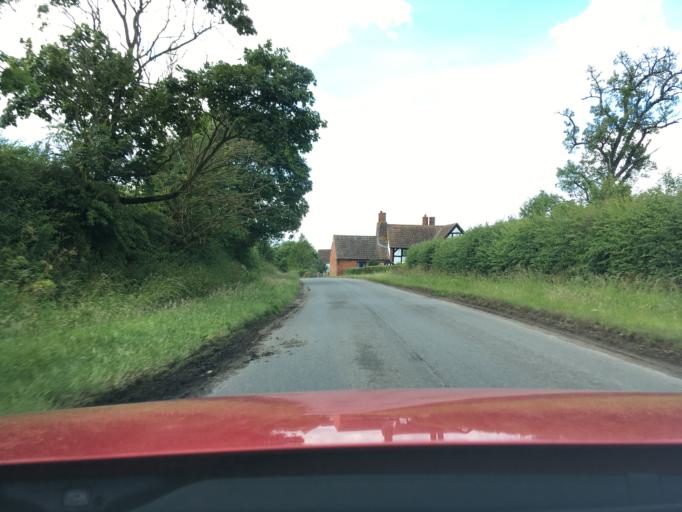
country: GB
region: England
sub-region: Gloucestershire
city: Gloucester
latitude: 51.8341
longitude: -2.3075
